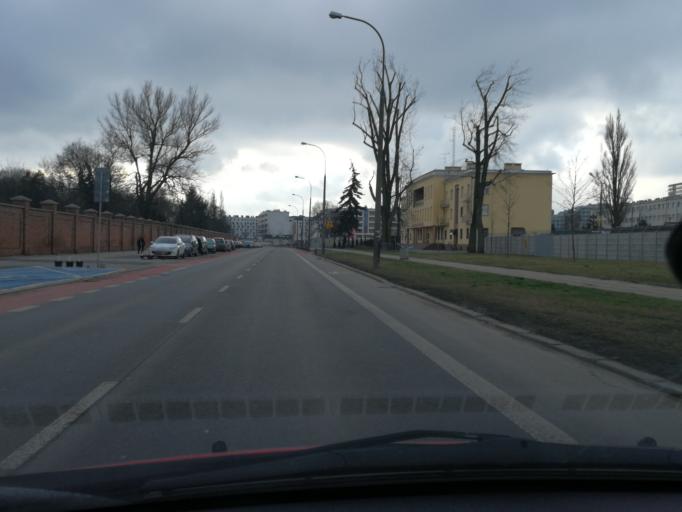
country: PL
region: Masovian Voivodeship
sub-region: Warszawa
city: Wola
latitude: 52.2504
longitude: 20.9649
